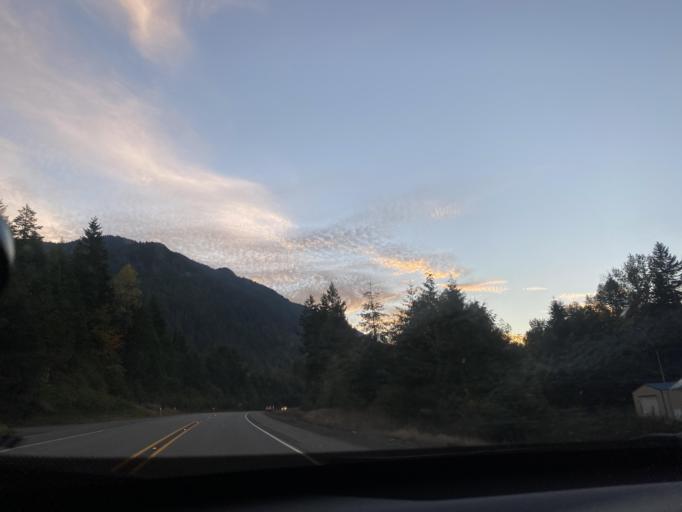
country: US
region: Washington
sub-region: Clallam County
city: Port Angeles
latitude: 48.0644
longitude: -123.5931
